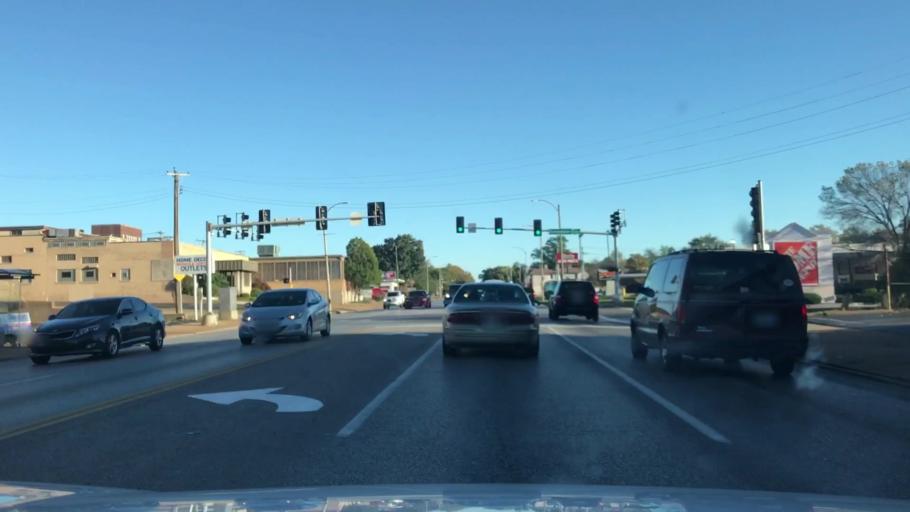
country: US
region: Missouri
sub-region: Saint Louis County
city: Maplewood
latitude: 38.6018
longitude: -90.2698
